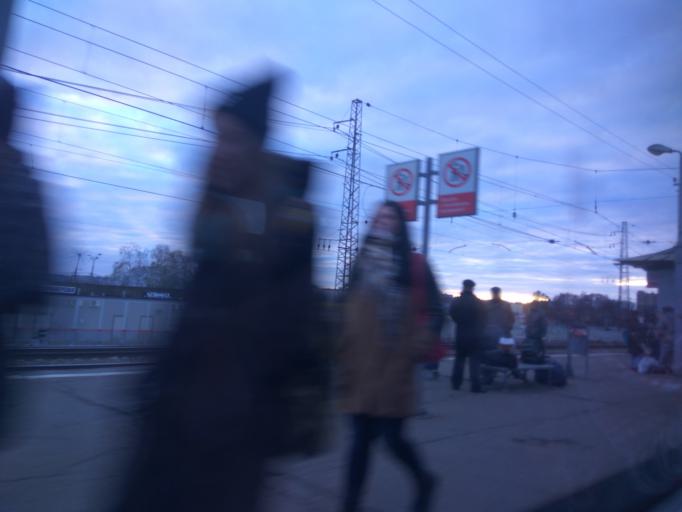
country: RU
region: Moskovskaya
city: Naro-Fominsk
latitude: 55.3832
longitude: 36.7519
